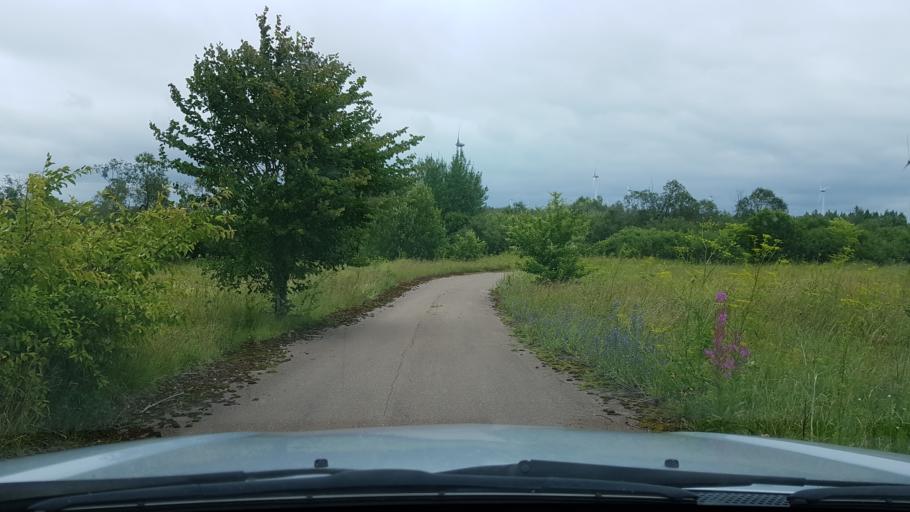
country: EE
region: Ida-Virumaa
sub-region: Narva-Joesuu linn
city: Narva-Joesuu
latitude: 59.3472
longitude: 28.0287
